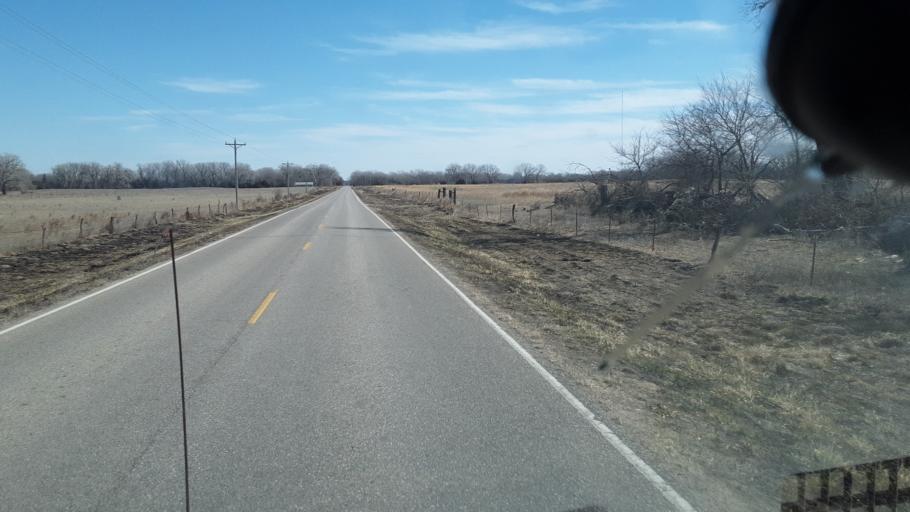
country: US
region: Kansas
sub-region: Reno County
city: Hutchinson
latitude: 38.1593
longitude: -97.8942
